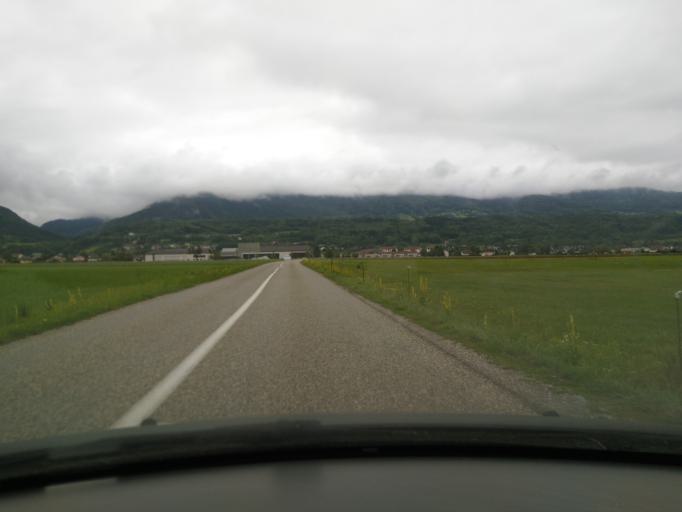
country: FR
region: Rhone-Alpes
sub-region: Departement de la Haute-Savoie
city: Amancy
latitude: 46.0705
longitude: 6.3650
